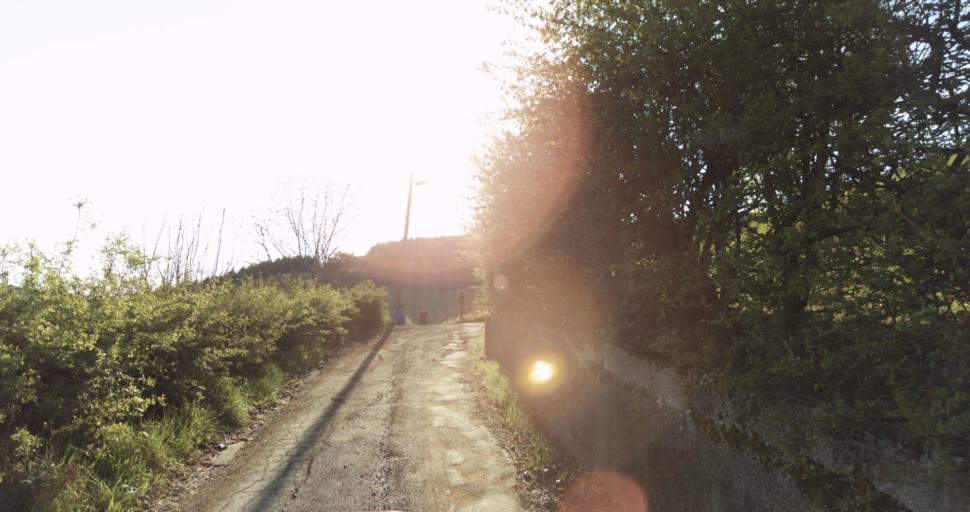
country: FR
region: Rhone-Alpes
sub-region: Departement du Rhone
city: Tarare
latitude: 45.8871
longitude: 4.4444
